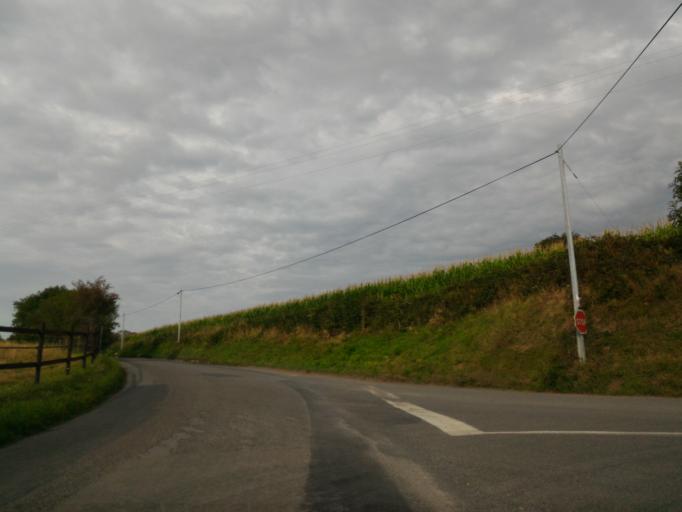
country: FR
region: Lower Normandy
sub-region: Departement de la Manche
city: Saint-Planchers
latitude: 48.7813
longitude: -1.5152
